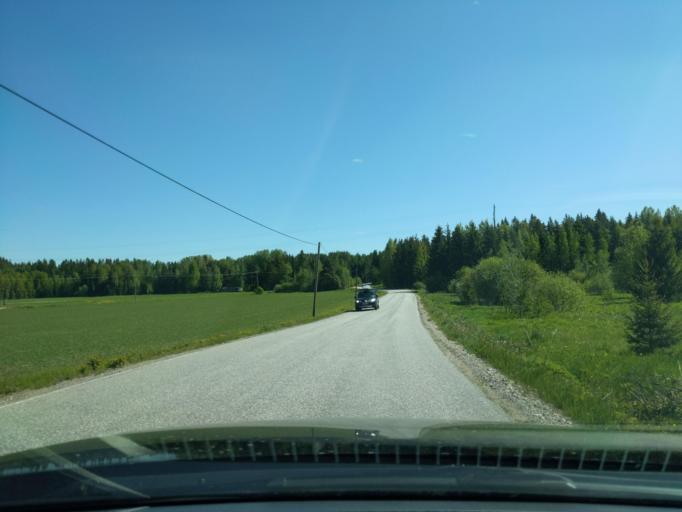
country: FI
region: Paijanne Tavastia
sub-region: Lahti
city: Lahti
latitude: 61.0612
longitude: 25.6769
